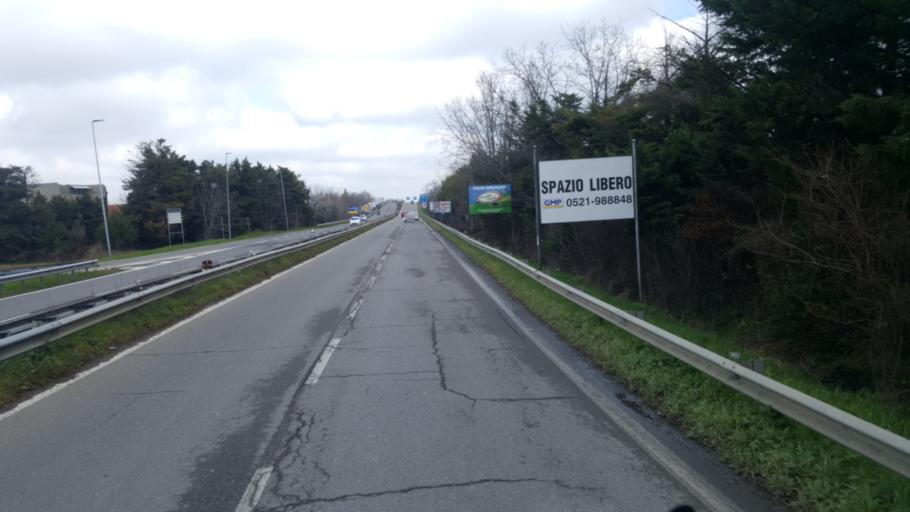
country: IT
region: Emilia-Romagna
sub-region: Provincia di Parma
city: Parma
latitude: 44.8096
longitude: 10.3011
